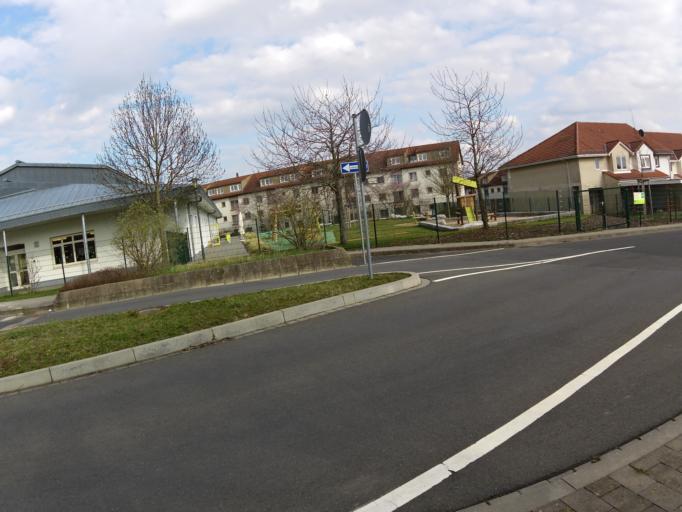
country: DE
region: Bavaria
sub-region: Regierungsbezirk Unterfranken
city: Kitzingen
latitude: 49.7388
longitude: 10.1321
